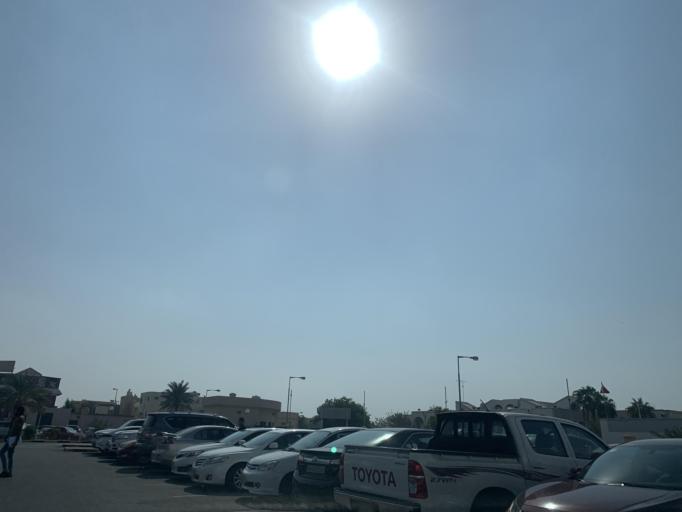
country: BH
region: Central Governorate
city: Madinat Hamad
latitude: 26.1324
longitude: 50.4967
